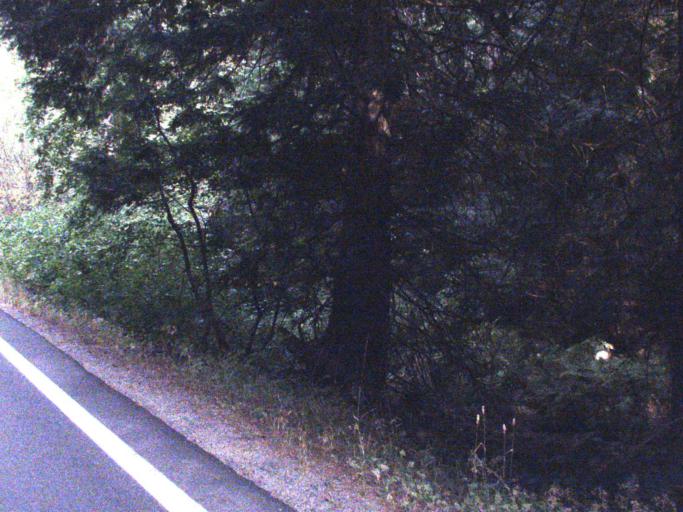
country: US
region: Washington
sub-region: Spokane County
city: Otis Orchards-East Farms
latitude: 47.8685
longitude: -117.1597
